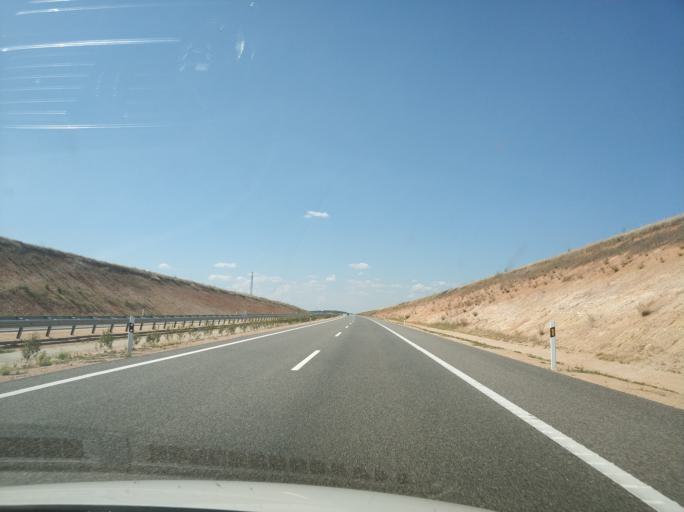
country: ES
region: Castille and Leon
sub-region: Provincia de Zamora
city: Montamarta
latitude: 41.6592
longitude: -5.7966
